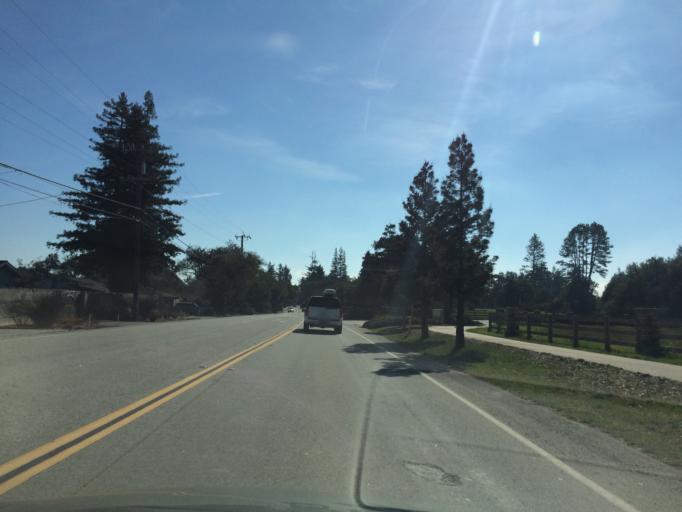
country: US
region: California
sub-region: Santa Cruz County
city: Pasatiempo
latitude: 37.0101
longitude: -122.0342
